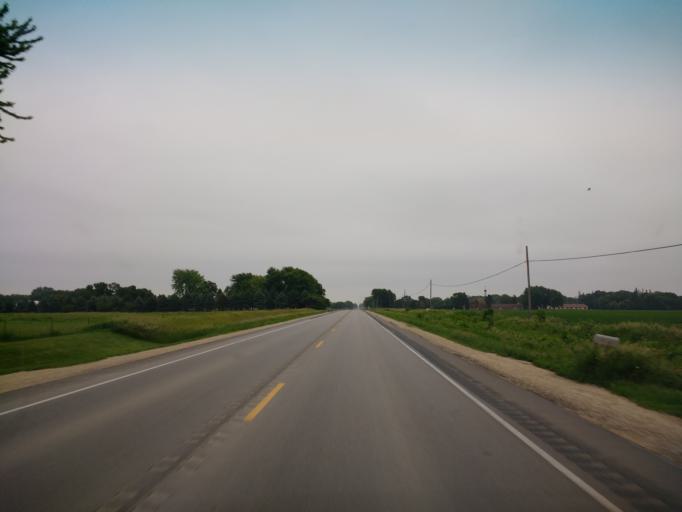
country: US
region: Iowa
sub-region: O'Brien County
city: Hartley
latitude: 43.1849
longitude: -95.4958
